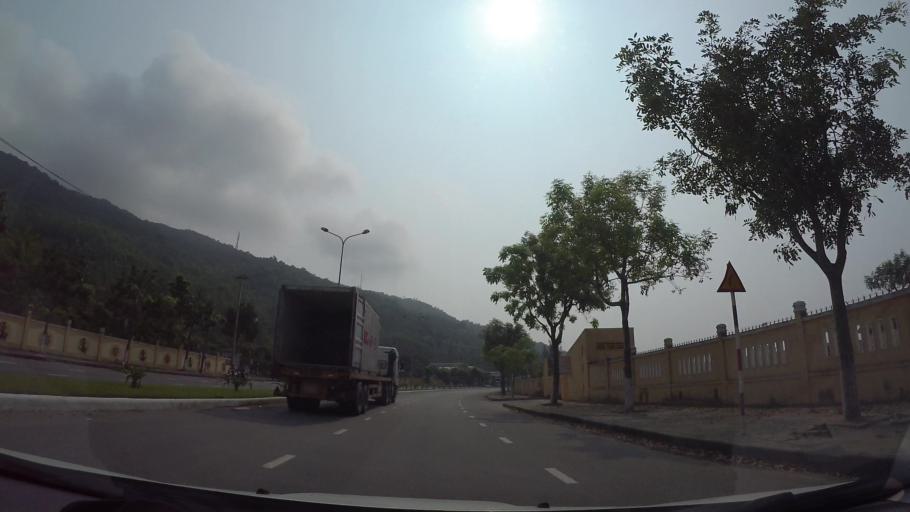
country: VN
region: Da Nang
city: Da Nang
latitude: 16.1139
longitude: 108.2424
